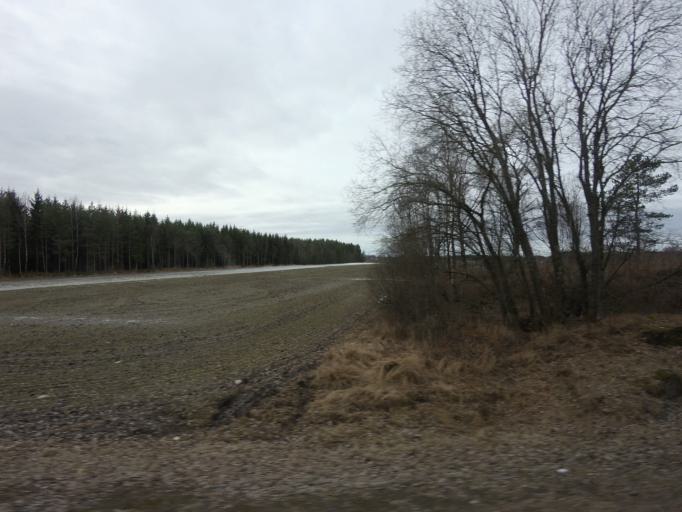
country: NO
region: Ostfold
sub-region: Trogstad
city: Skjonhaug
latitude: 59.6811
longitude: 11.3018
